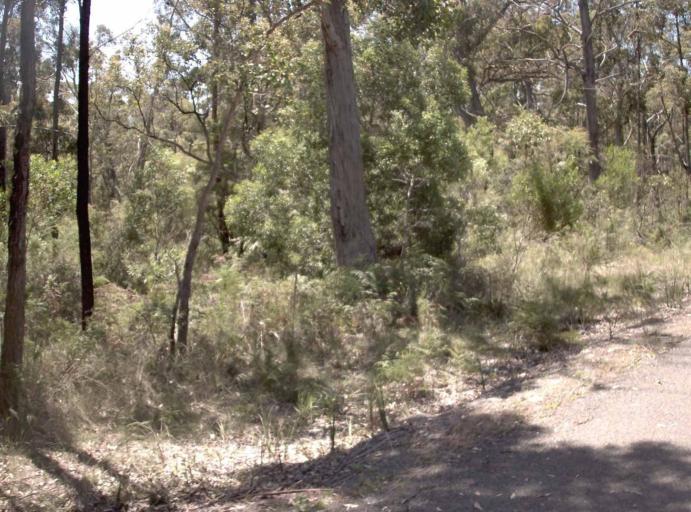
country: AU
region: Victoria
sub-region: East Gippsland
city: Lakes Entrance
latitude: -37.7524
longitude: 148.2023
